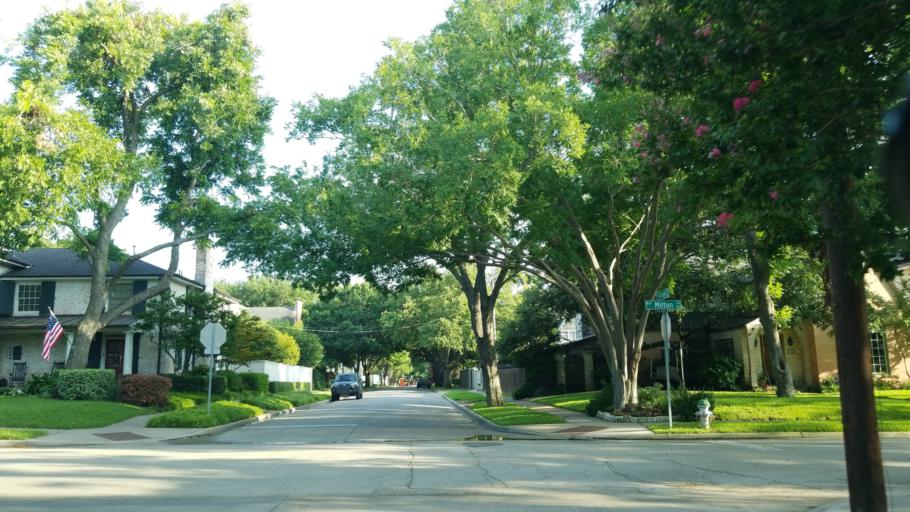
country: US
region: Texas
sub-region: Dallas County
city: University Park
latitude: 32.8484
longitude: -96.7928
